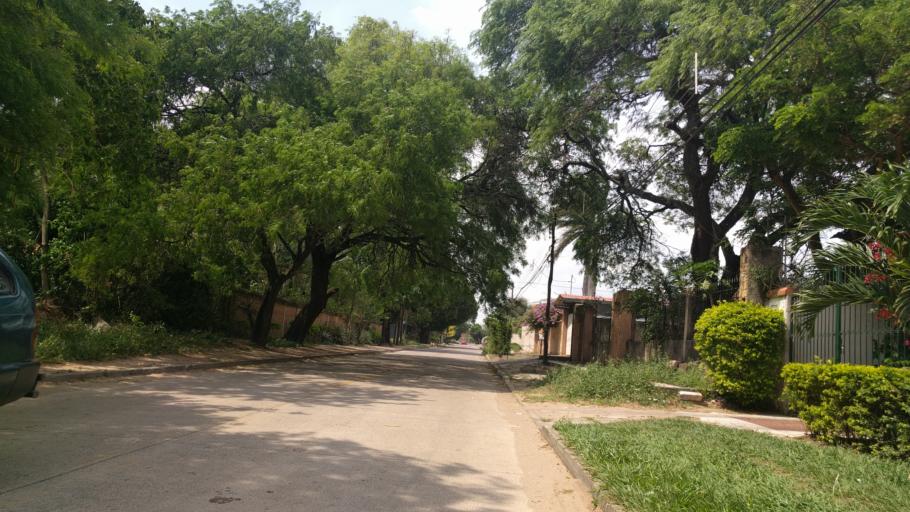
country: BO
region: Santa Cruz
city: Santa Cruz de la Sierra
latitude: -17.7971
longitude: -63.2224
